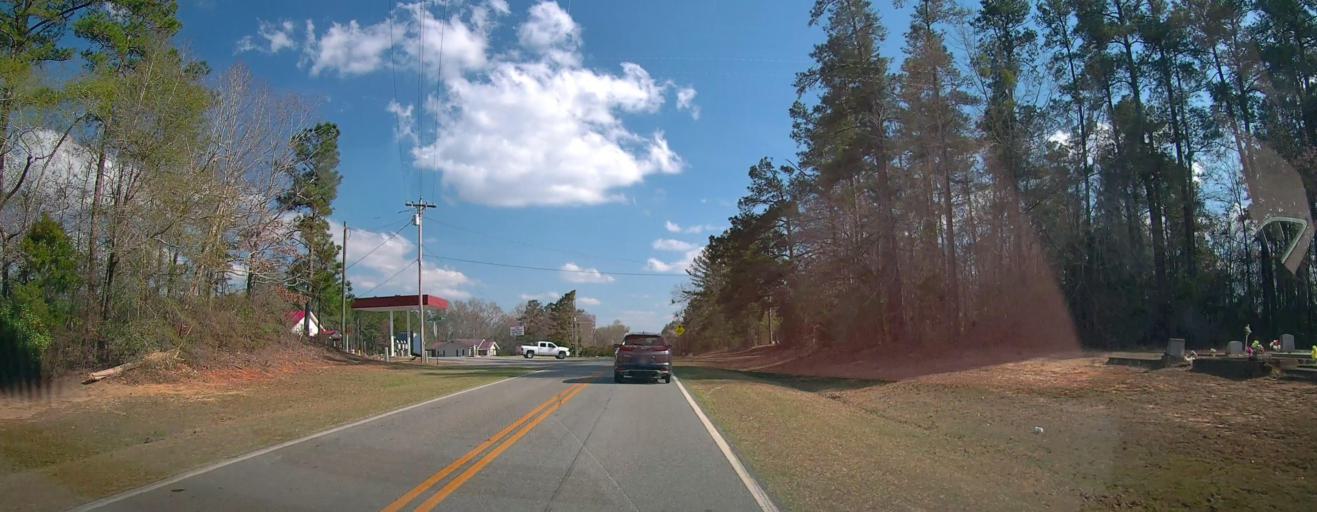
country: US
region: Georgia
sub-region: Laurens County
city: Dublin
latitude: 32.6185
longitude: -83.0866
